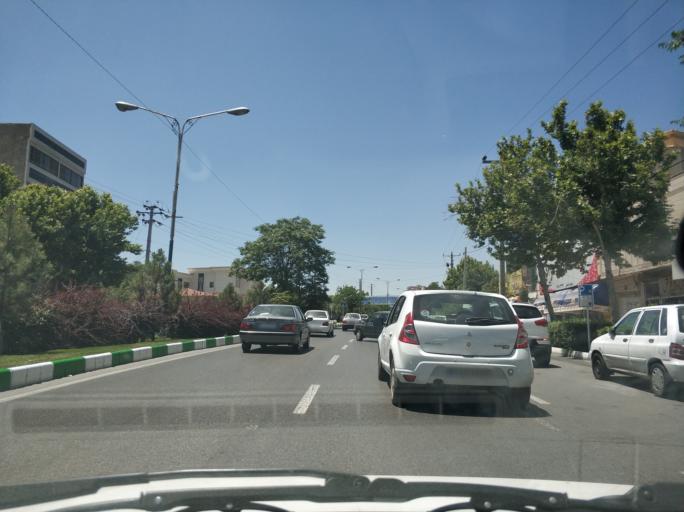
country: IR
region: Razavi Khorasan
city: Mashhad
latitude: 36.3129
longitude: 59.4924
